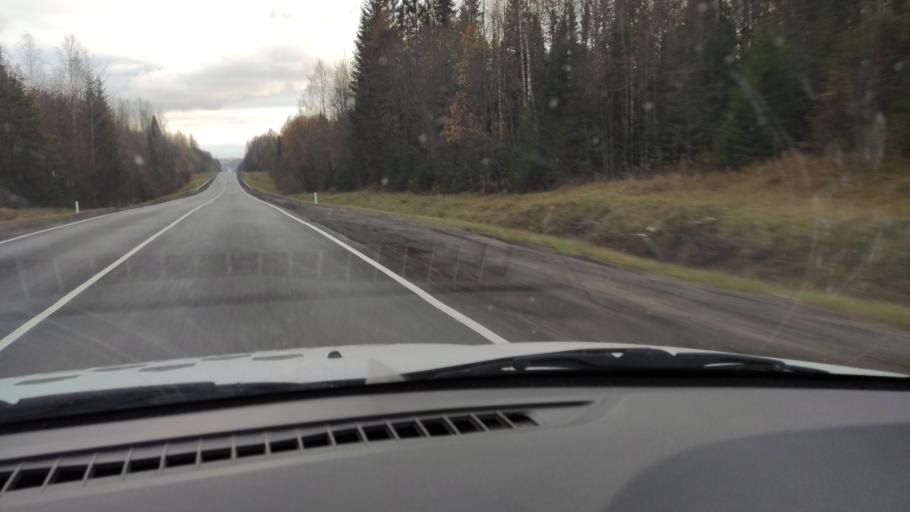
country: RU
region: Kirov
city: Omutninsk
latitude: 58.7450
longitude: 52.0636
